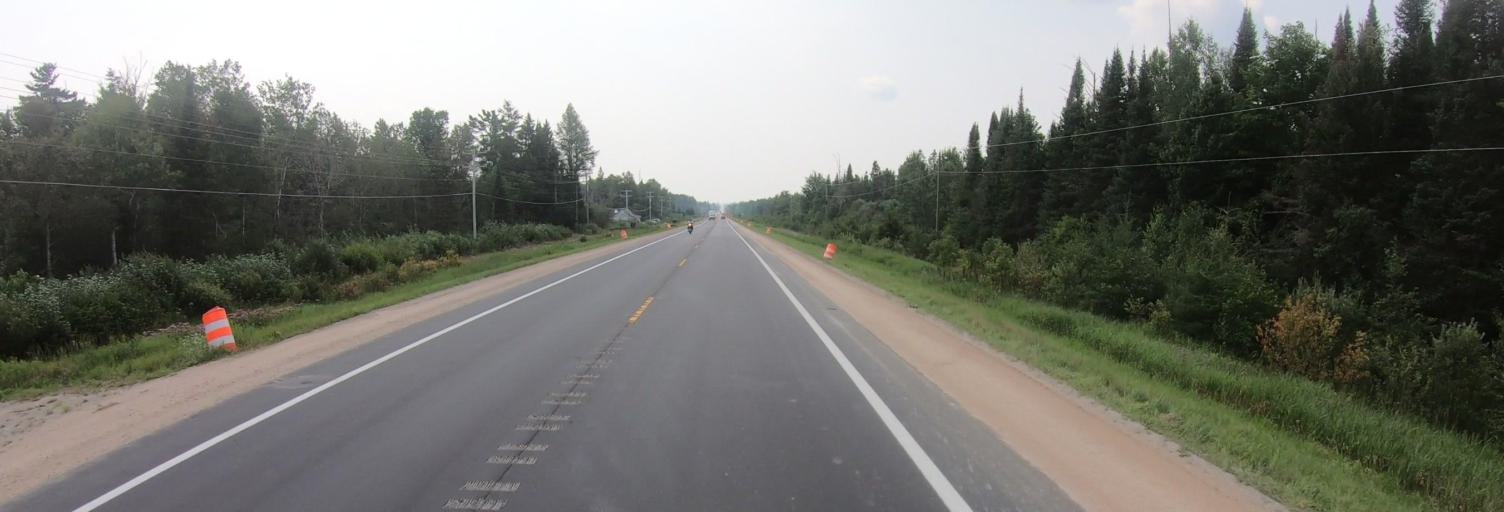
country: US
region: Michigan
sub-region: Luce County
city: Newberry
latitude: 46.3838
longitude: -85.5099
